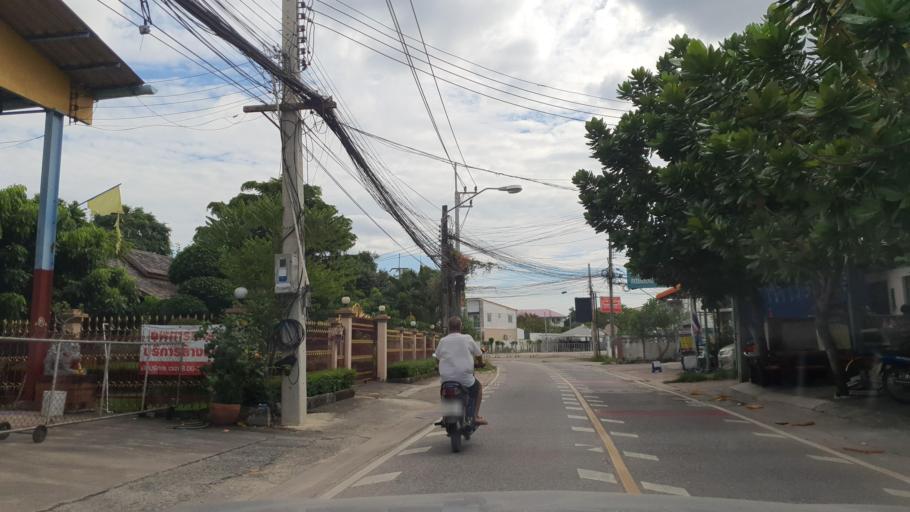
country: TH
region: Chon Buri
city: Phatthaya
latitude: 12.9562
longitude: 100.9125
